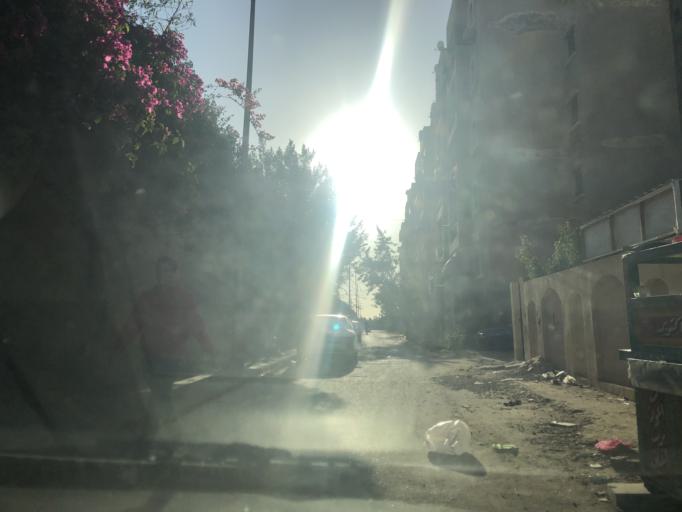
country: EG
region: Al Jizah
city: Al Jizah
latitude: 29.9883
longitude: 31.0980
